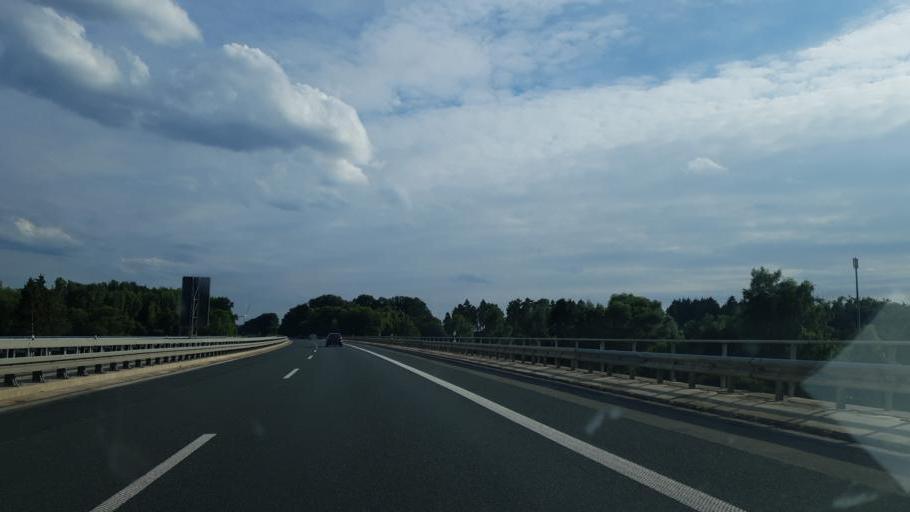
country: DE
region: Lower Saxony
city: Holle
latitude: 52.1026
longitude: 10.1827
